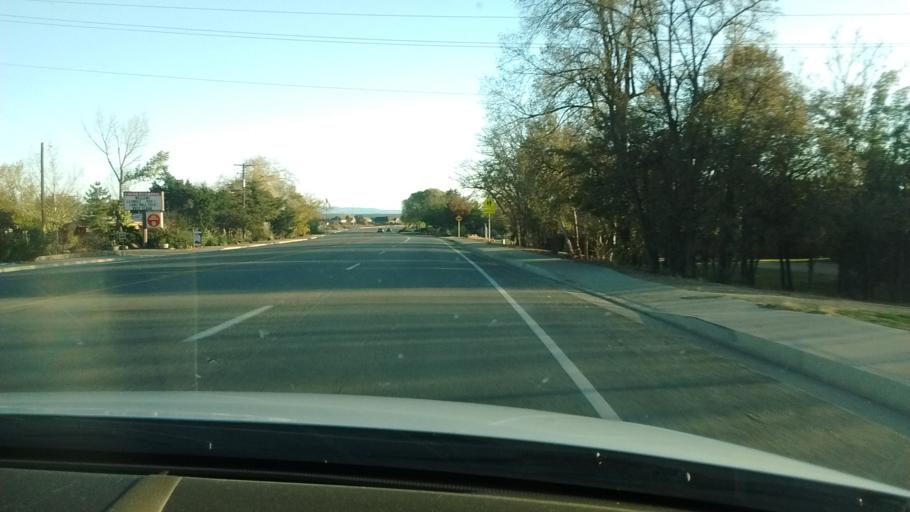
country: US
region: Utah
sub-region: Kane County
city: Kanab
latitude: 37.0405
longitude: -112.5263
